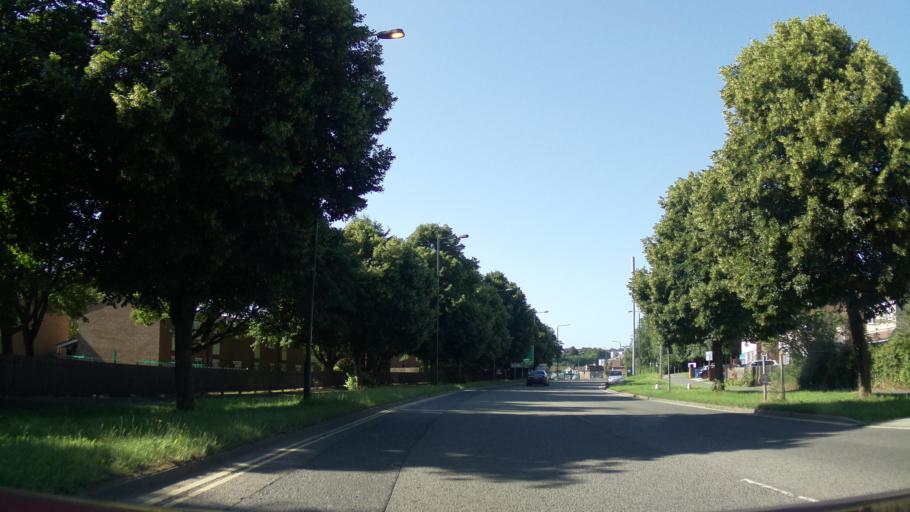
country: GB
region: England
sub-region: Derby
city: Derby
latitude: 52.9168
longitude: -1.5075
